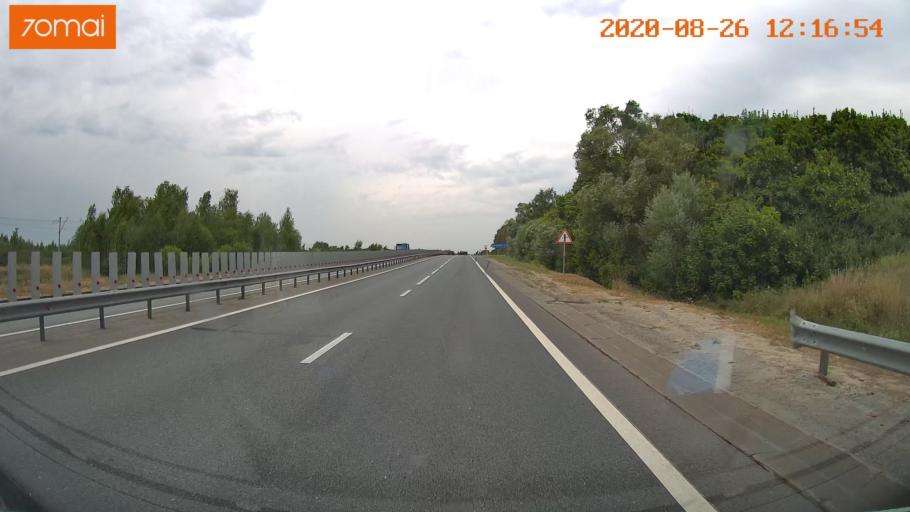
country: RU
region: Rjazan
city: Murmino
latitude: 54.4532
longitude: 40.0341
